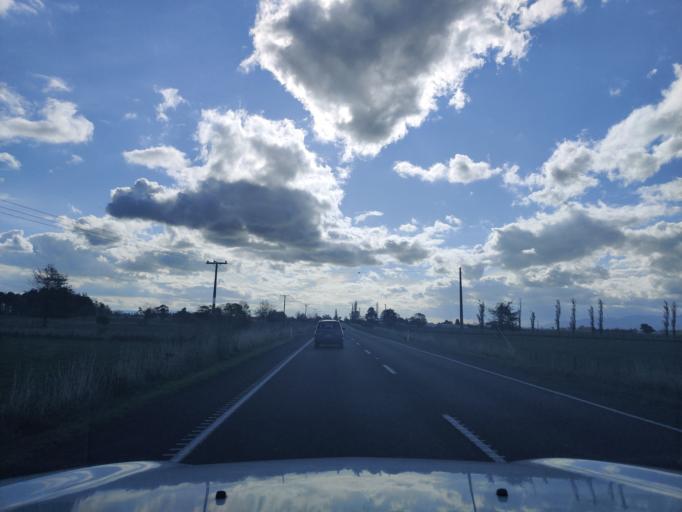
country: NZ
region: Waikato
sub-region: Hauraki District
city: Ngatea
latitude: -37.2921
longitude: 175.5507
